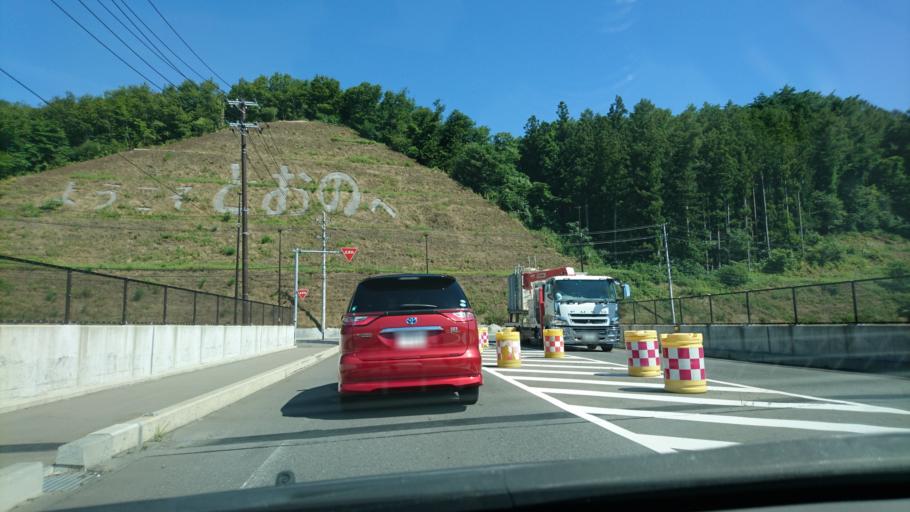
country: JP
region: Iwate
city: Tono
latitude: 39.3319
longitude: 141.5093
